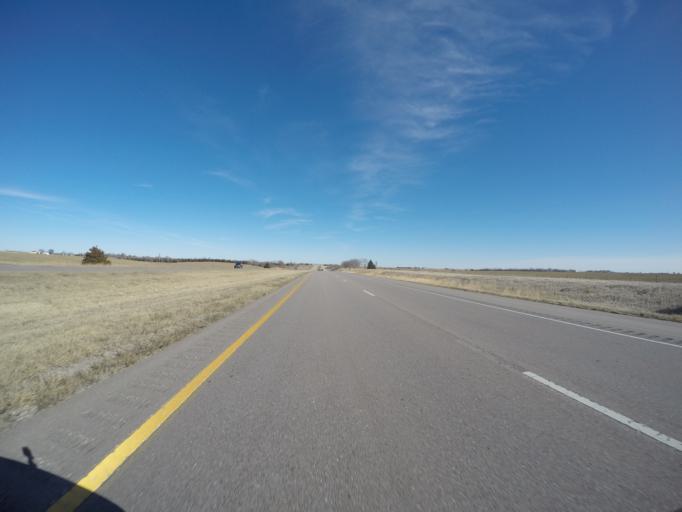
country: US
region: Nebraska
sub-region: Saline County
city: Friend
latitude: 40.8222
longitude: -97.2726
